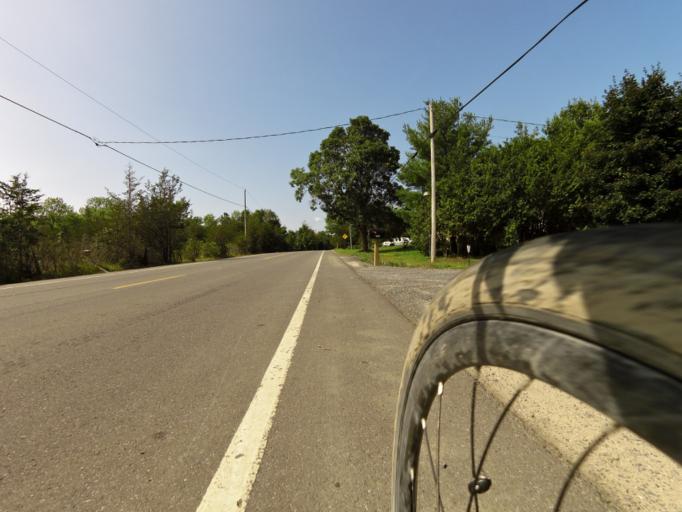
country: CA
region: Ontario
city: Skatepark
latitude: 44.2532
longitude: -76.7228
